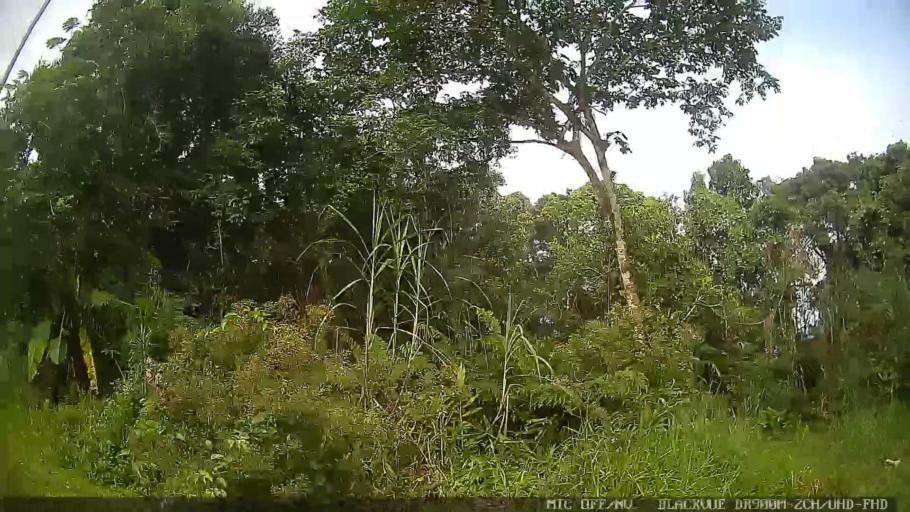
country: BR
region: Sao Paulo
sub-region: Peruibe
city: Peruibe
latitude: -24.2181
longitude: -46.9299
